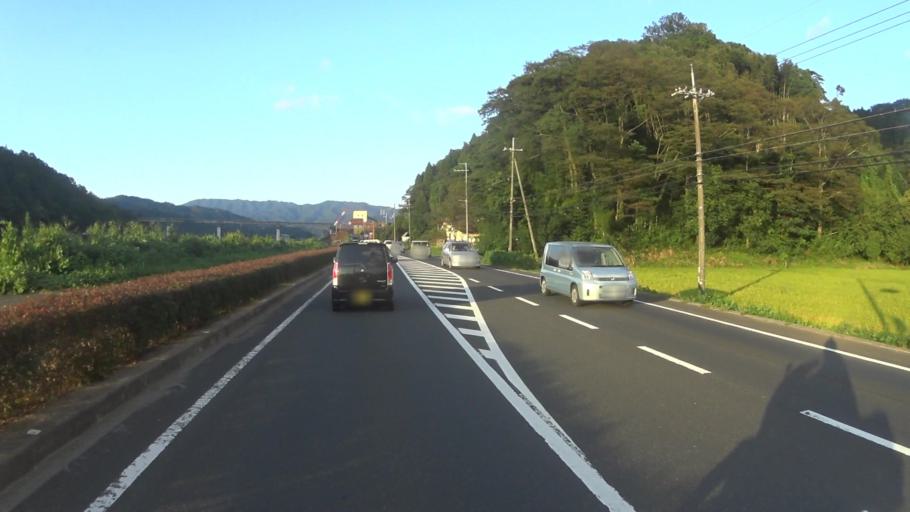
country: JP
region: Kyoto
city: Miyazu
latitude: 35.5456
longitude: 135.1345
